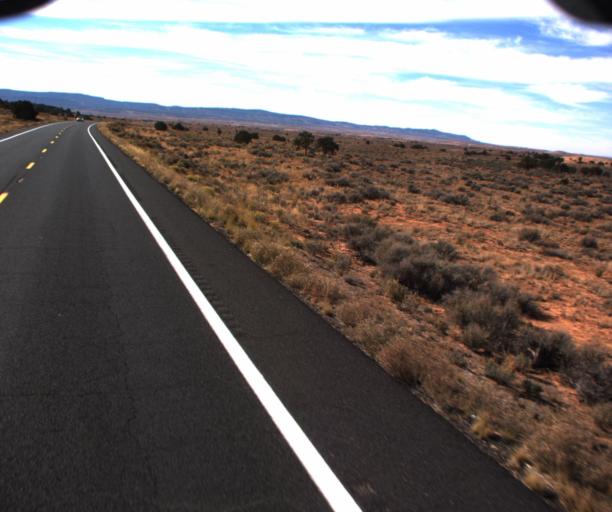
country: US
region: Arizona
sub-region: Coconino County
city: Kaibito
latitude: 36.5299
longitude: -110.7014
